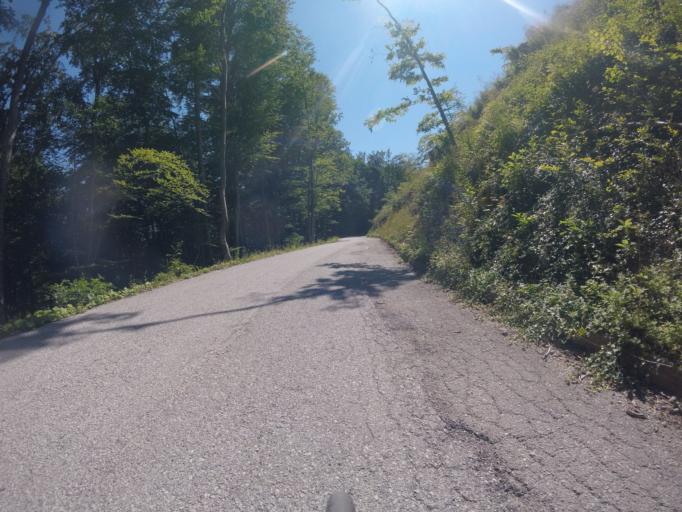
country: SI
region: Kostanjevica na Krki
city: Kostanjevica na Krki
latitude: 45.8147
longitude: 15.5124
